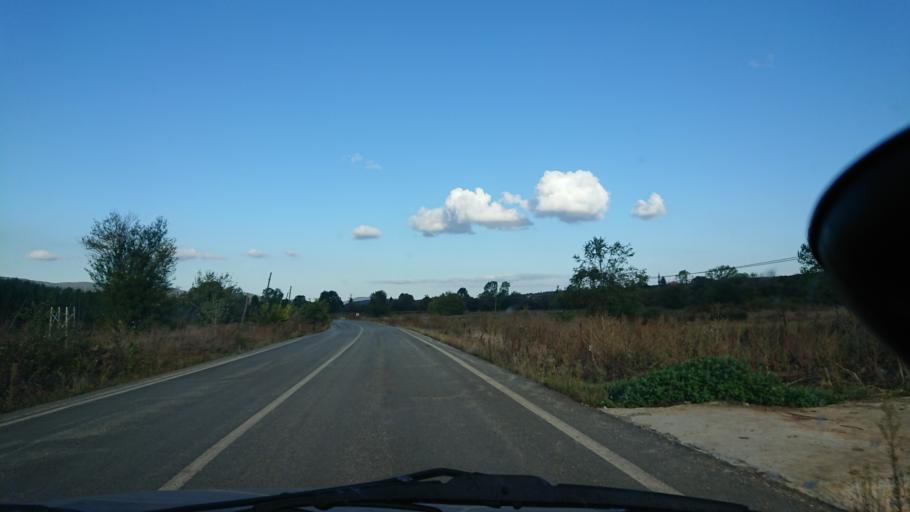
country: TR
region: Bilecik
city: Pazaryeri
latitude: 40.0123
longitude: 29.8218
